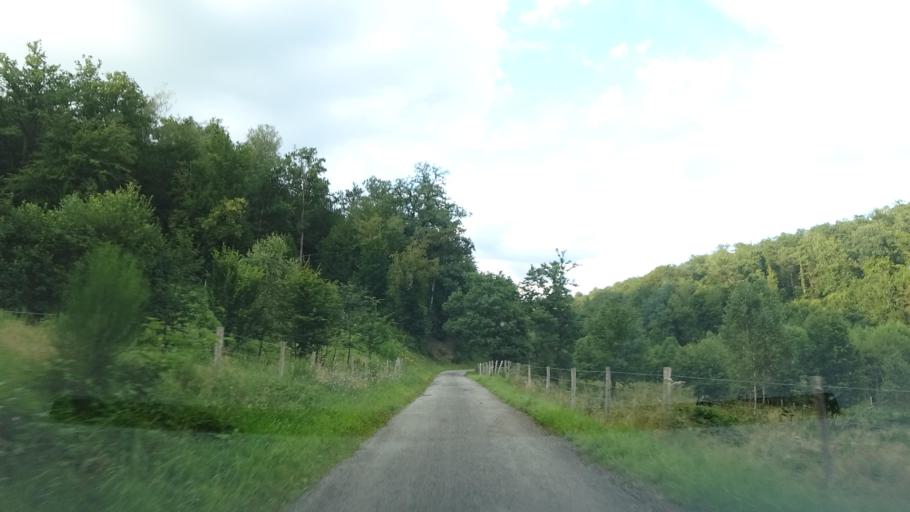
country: BE
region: Wallonia
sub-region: Province du Luxembourg
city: Herbeumont
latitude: 49.7787
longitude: 5.2570
